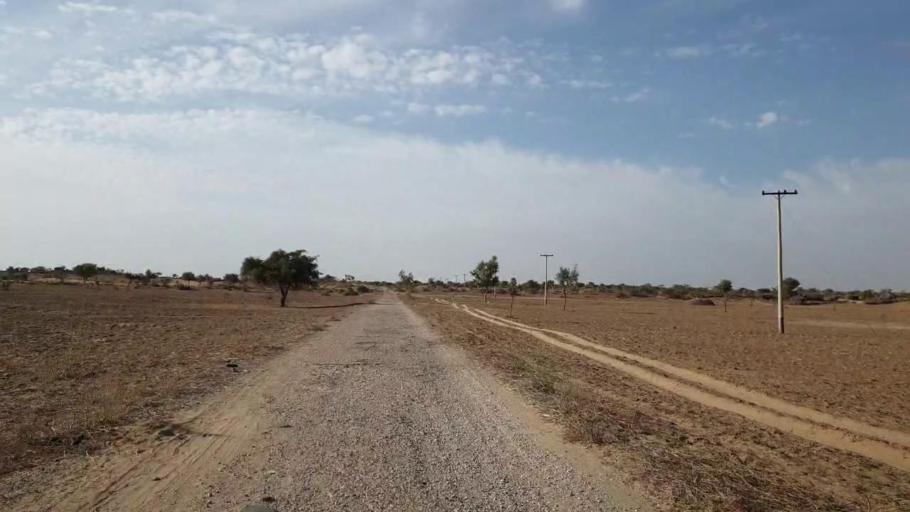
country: PK
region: Sindh
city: Nabisar
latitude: 25.0487
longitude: 69.9710
